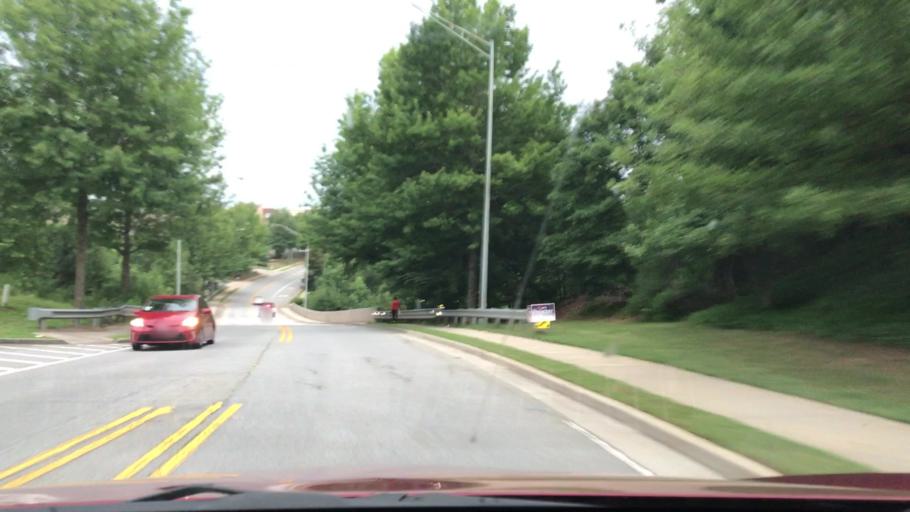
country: US
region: Georgia
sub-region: Gwinnett County
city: Sugar Hill
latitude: 34.0612
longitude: -83.9956
